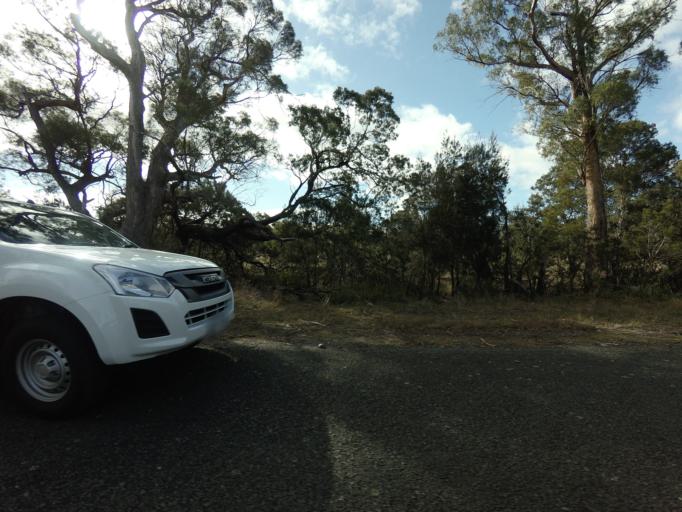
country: AU
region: Tasmania
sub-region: Sorell
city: Sorell
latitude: -42.3254
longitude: 147.9599
